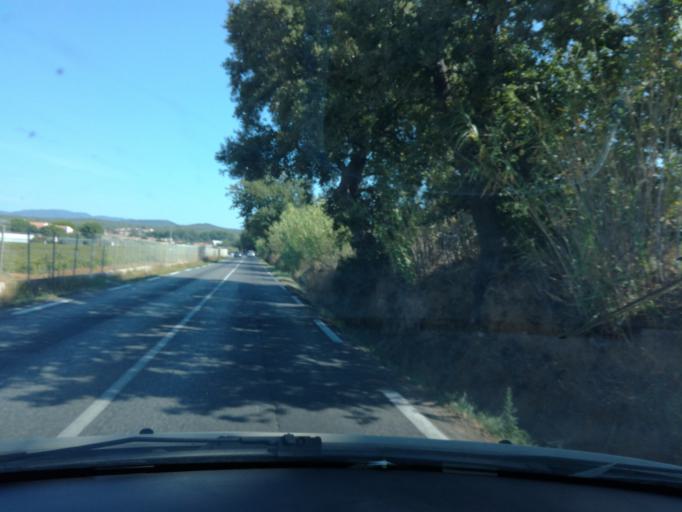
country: FR
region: Provence-Alpes-Cote d'Azur
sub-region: Departement du Var
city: La Crau
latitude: 43.1388
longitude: 6.0798
